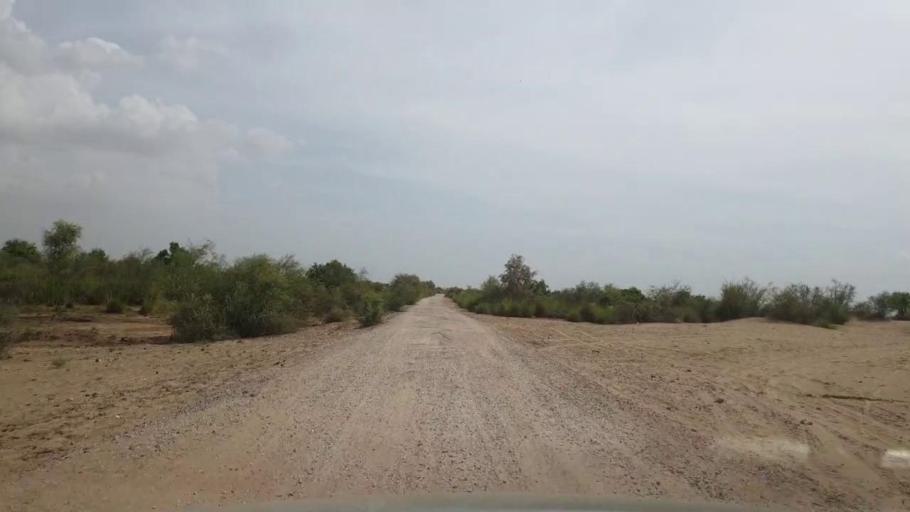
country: PK
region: Sindh
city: Bozdar
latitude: 27.1031
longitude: 69.0198
